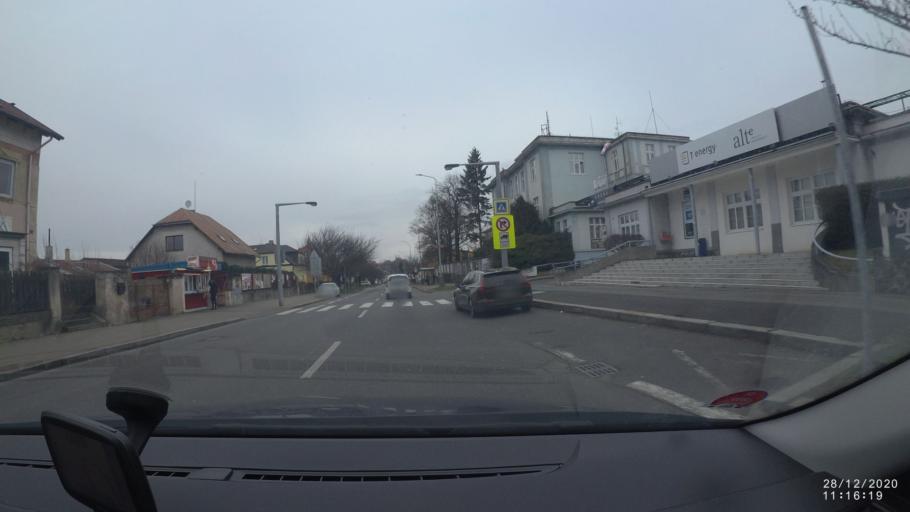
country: CZ
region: Praha
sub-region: Praha 18
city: Letnany
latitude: 50.1350
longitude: 14.5140
